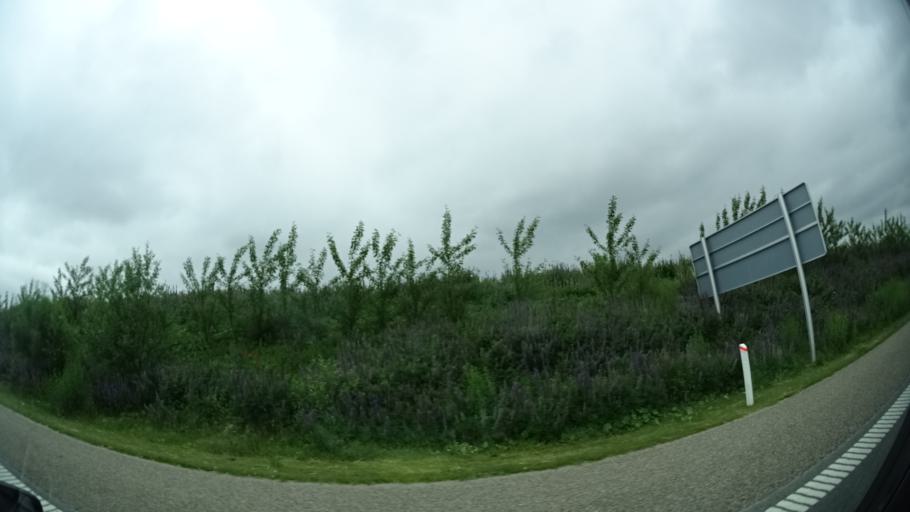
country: DK
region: Central Jutland
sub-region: Arhus Kommune
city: Hjortshoj
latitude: 56.2363
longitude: 10.2731
